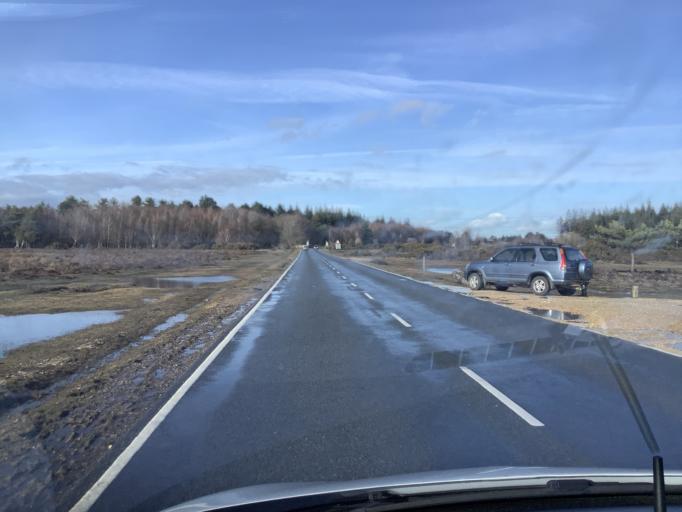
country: GB
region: England
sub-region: Hampshire
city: Hythe
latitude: 50.8452
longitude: -1.4243
